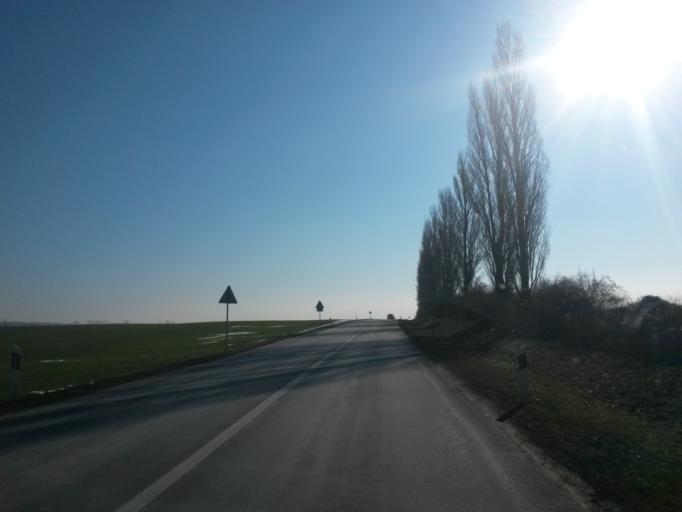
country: HR
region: Osjecko-Baranjska
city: Dalj
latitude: 45.5176
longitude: 18.9158
